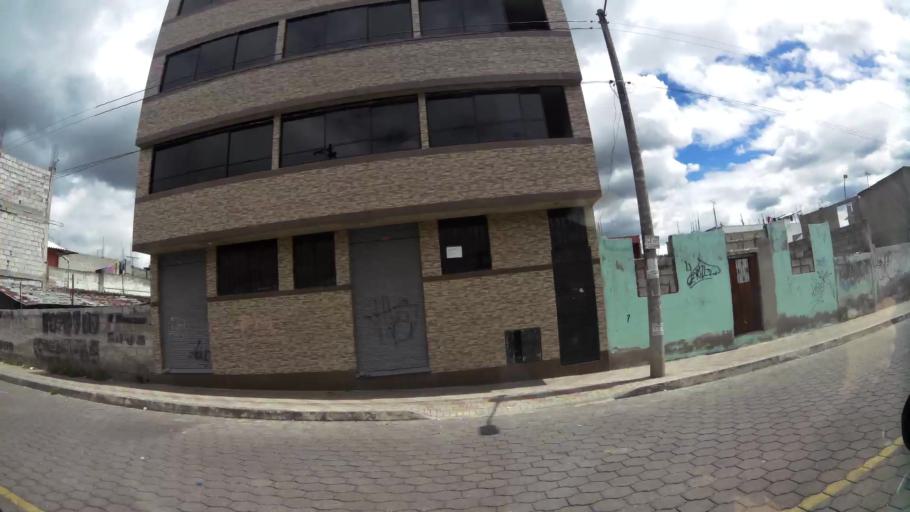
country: EC
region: Pichincha
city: Sangolqui
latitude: -0.3372
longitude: -78.5453
